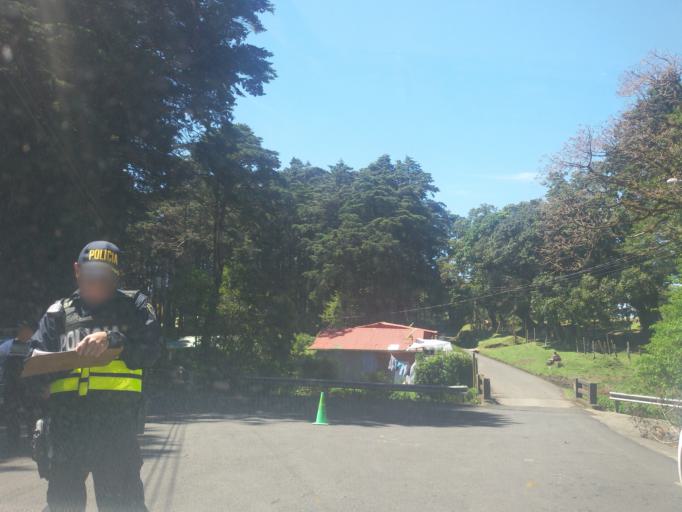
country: CR
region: Heredia
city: San Josecito
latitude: 10.0746
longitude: -84.0972
